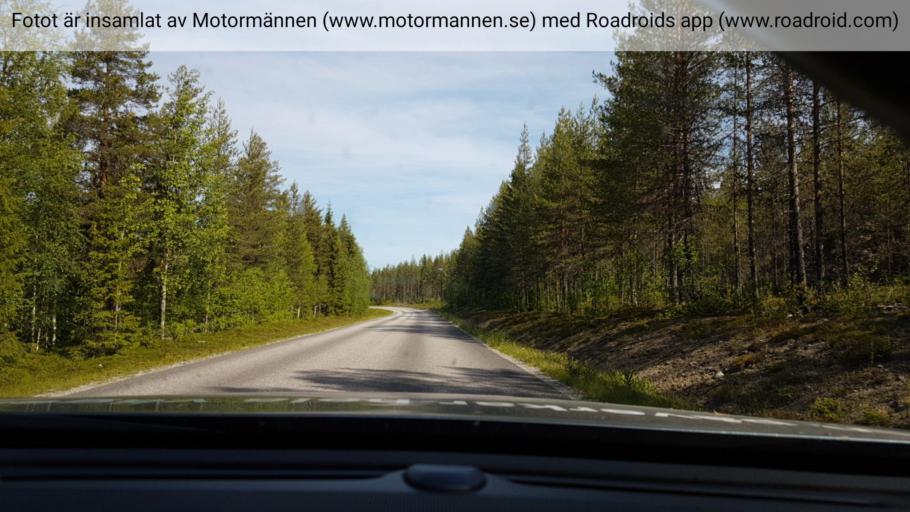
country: SE
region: Vaesterbotten
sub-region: Vilhelmina Kommun
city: Sjoberg
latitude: 64.4700
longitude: 15.9504
